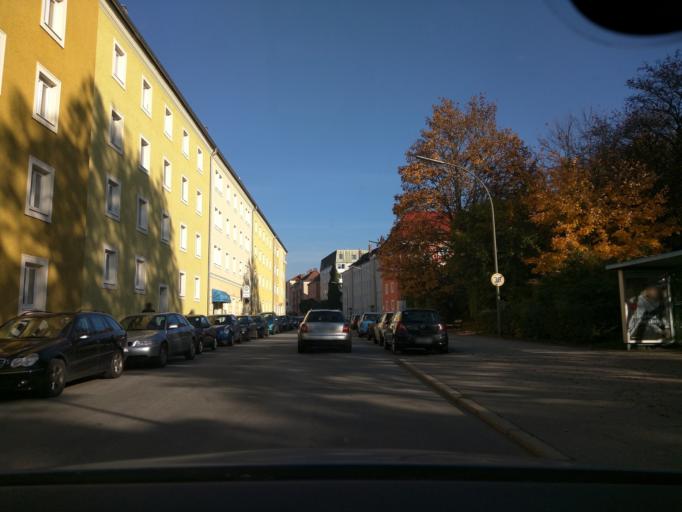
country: DE
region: Bavaria
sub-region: Lower Bavaria
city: Passau
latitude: 48.5711
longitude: 13.4396
